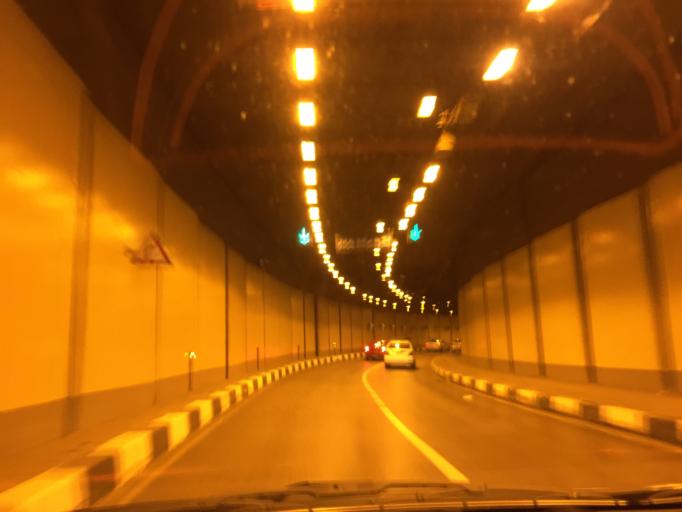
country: EG
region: Muhafazat al Qahirah
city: Cairo
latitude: 30.0456
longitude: 31.2711
